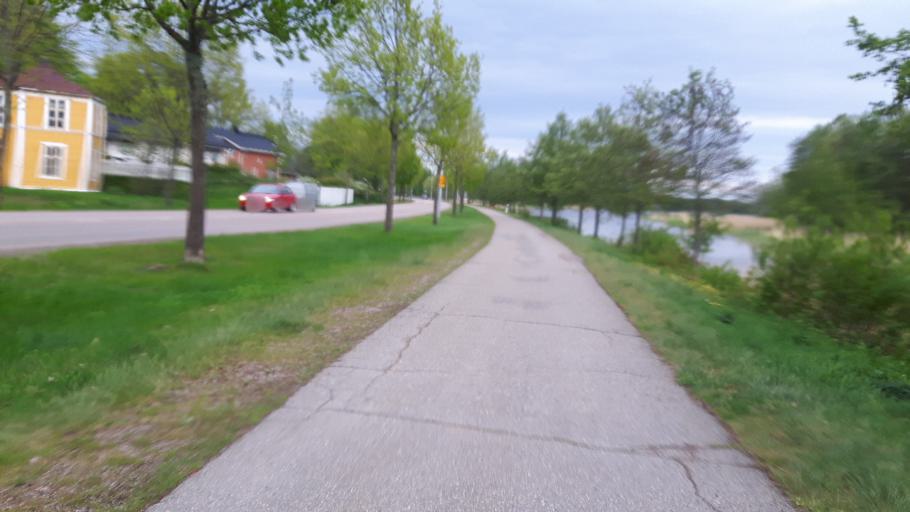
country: FI
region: Kymenlaakso
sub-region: Kotka-Hamina
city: Hamina
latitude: 60.5628
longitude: 27.2056
